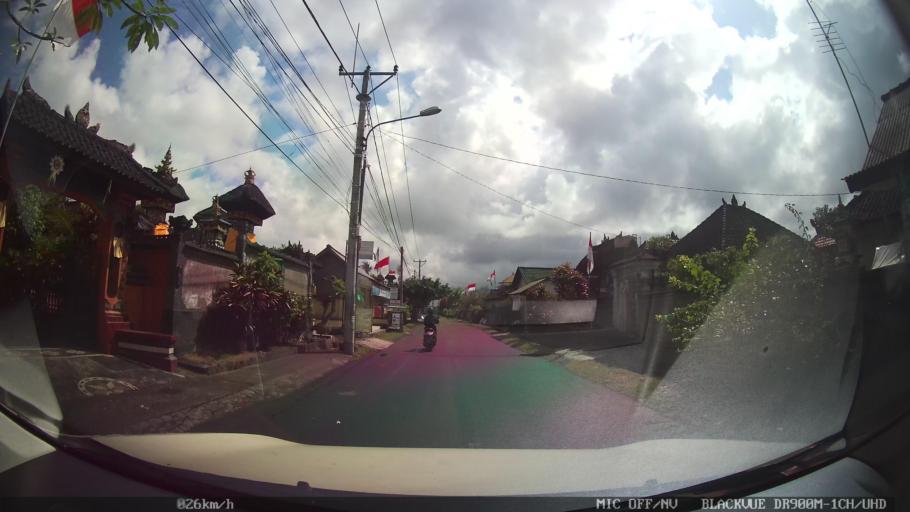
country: ID
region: Bali
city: Banjar Karangsuling
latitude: -8.6007
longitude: 115.2024
